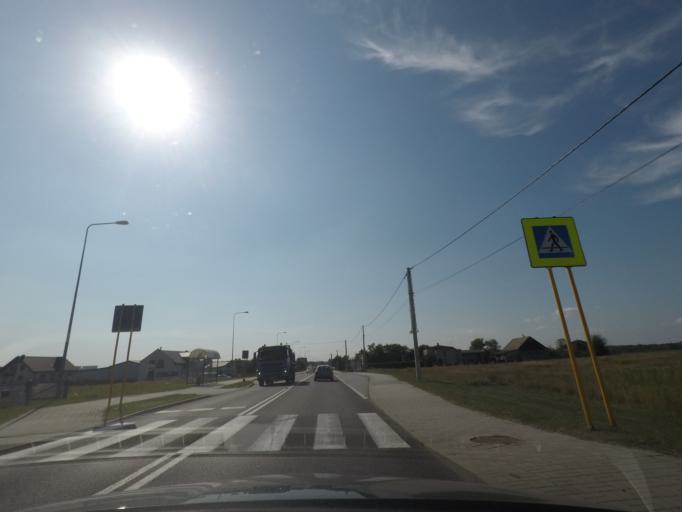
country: PL
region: Silesian Voivodeship
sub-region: Powiat pszczynski
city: Rudziczka
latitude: 50.0394
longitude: 18.7326
